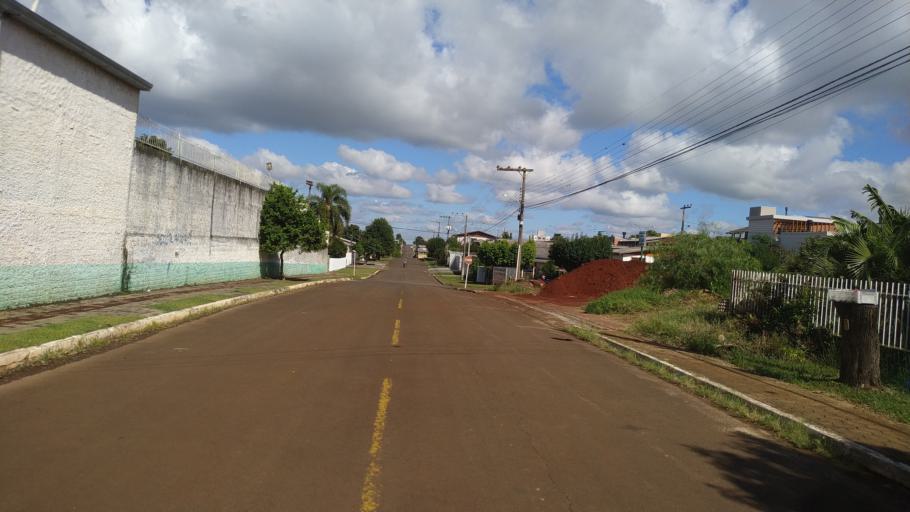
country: BR
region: Santa Catarina
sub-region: Chapeco
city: Chapeco
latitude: -27.0986
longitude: -52.6342
